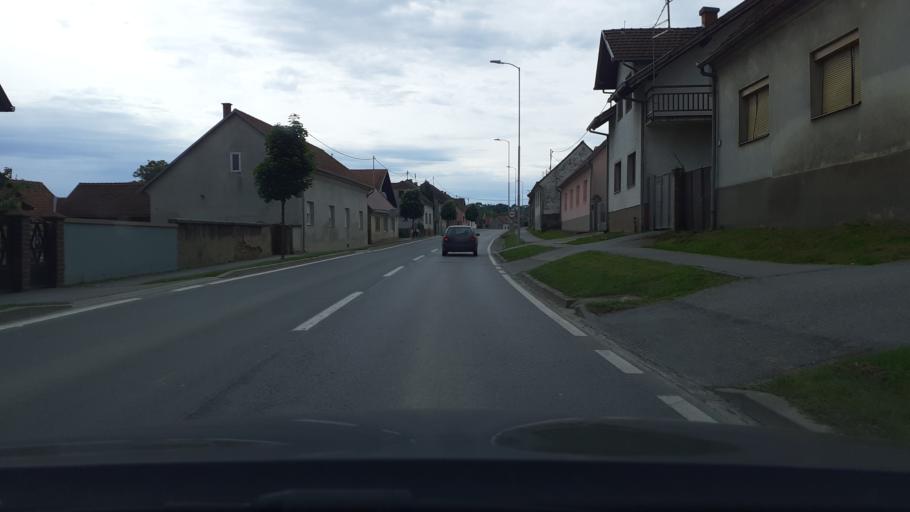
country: HR
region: Pozesko-Slavonska
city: Pleternica
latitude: 45.2914
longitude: 17.8002
